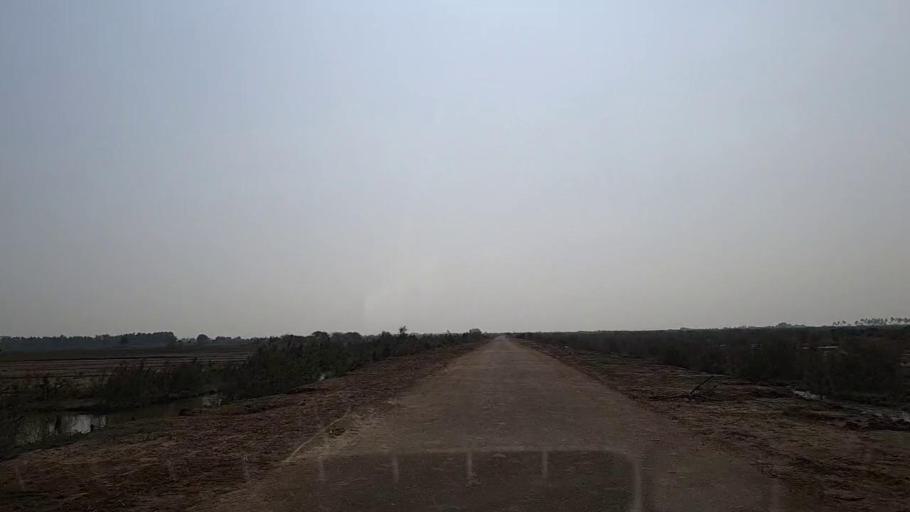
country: PK
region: Sindh
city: Mirpur Sakro
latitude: 24.6609
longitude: 67.6931
